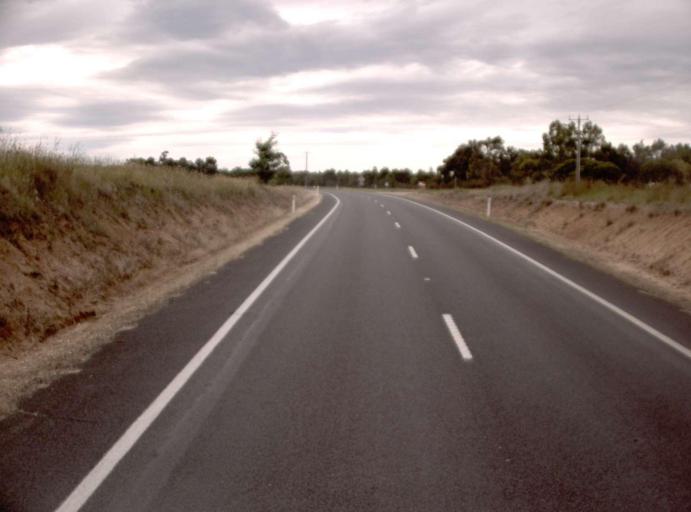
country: AU
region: Victoria
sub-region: Wellington
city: Sale
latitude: -38.2882
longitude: 147.0362
